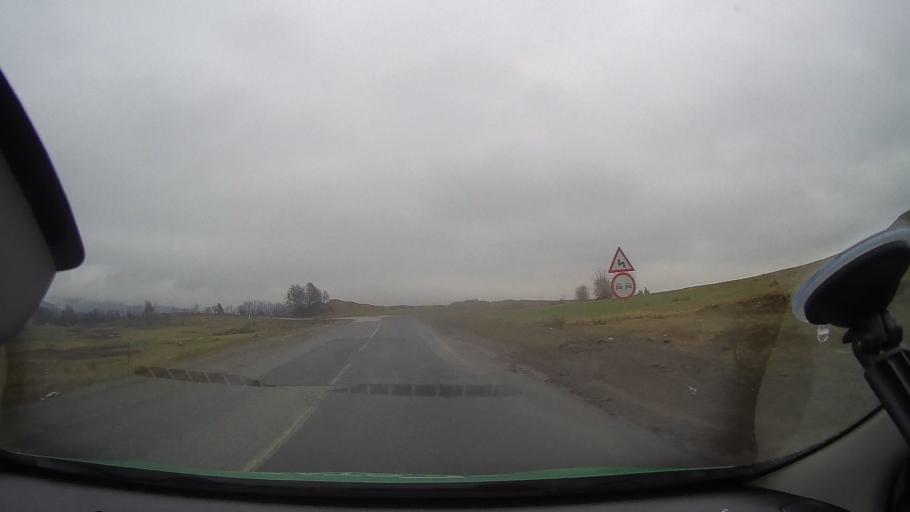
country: RO
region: Arad
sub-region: Comuna Halmagiu
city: Halmagiu
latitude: 46.2818
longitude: 22.5798
